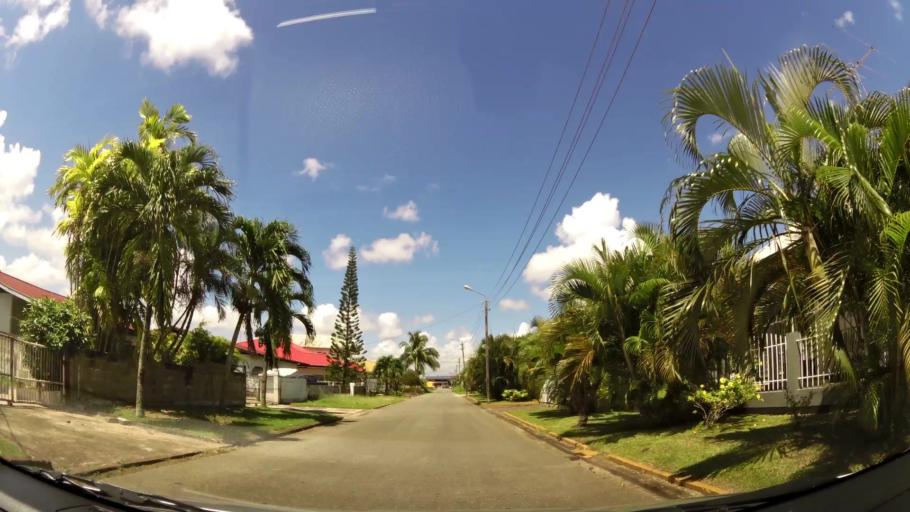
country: SR
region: Paramaribo
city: Paramaribo
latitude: 5.8621
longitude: -55.1448
